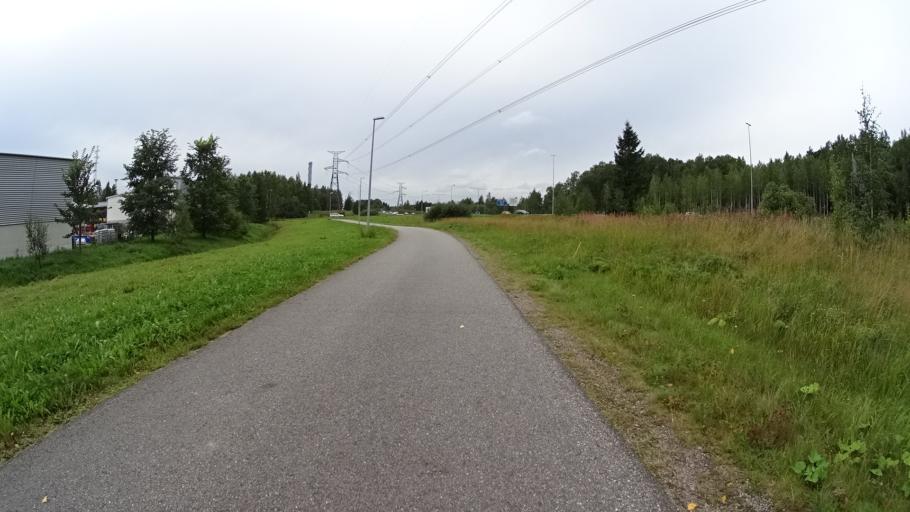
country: FI
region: Uusimaa
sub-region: Helsinki
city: Kilo
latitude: 60.2864
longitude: 24.8343
